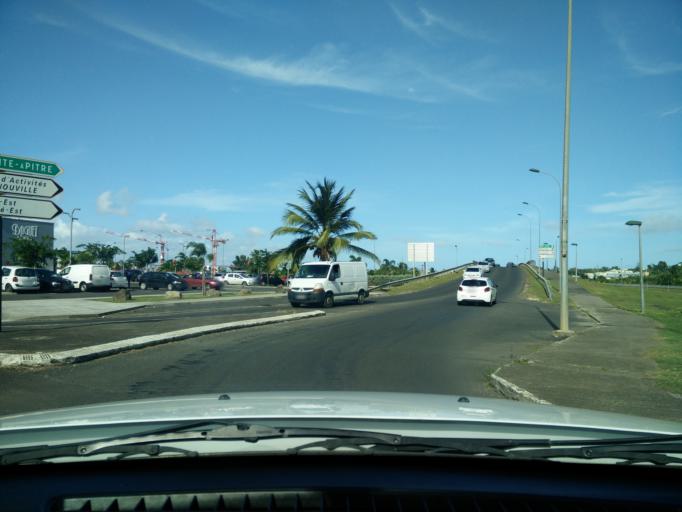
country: GP
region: Guadeloupe
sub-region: Guadeloupe
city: Petit-Bourg
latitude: 16.2026
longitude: -61.6069
